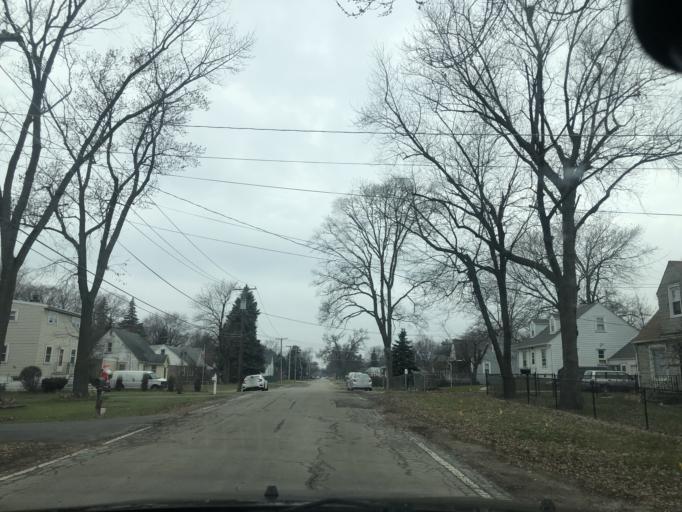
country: US
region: Illinois
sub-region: Cook County
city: Northlake
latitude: 41.9345
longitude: -87.8947
